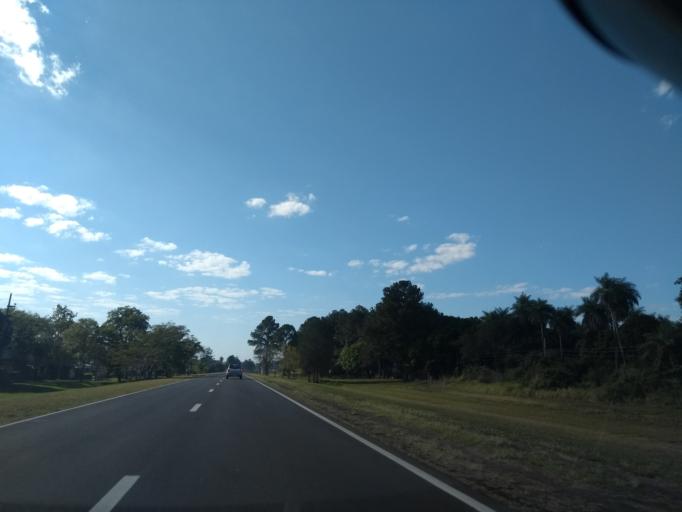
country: AR
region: Corrientes
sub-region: Departamento de Itati
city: Itati
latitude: -27.3661
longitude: -58.3088
